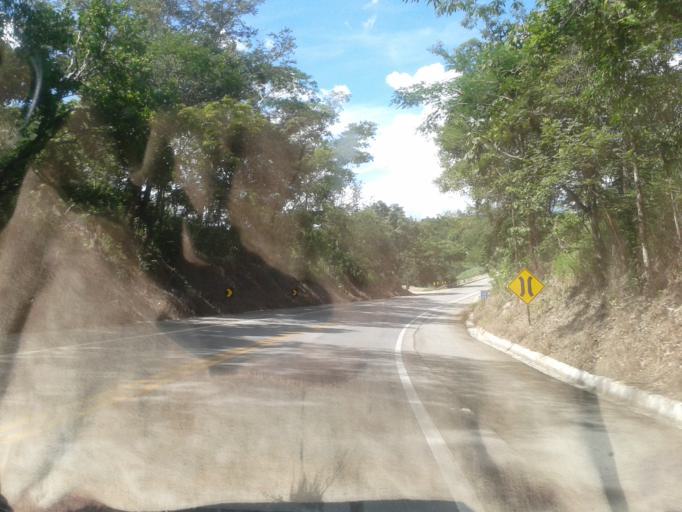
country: BR
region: Goias
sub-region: Goias
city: Goias
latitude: -15.7884
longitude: -50.1317
